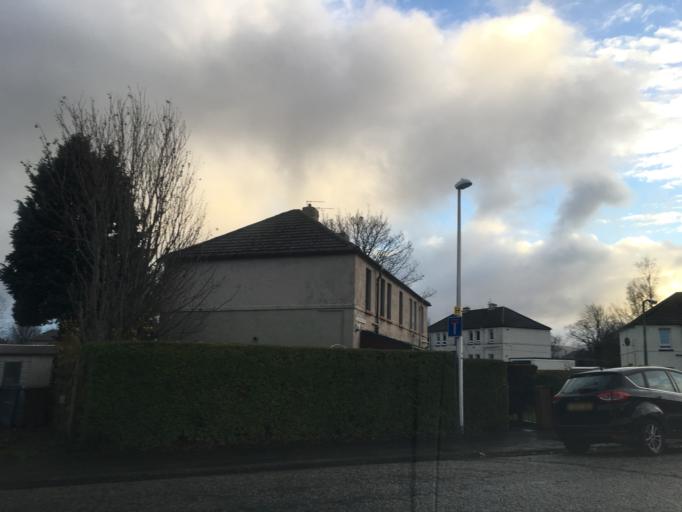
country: GB
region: Scotland
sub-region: Edinburgh
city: Colinton
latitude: 55.9395
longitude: -3.2554
